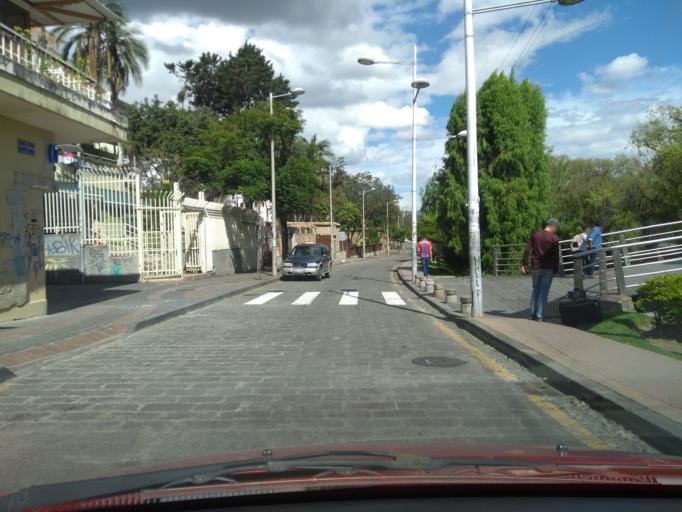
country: EC
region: Azuay
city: Cuenca
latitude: -2.9021
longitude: -79.0048
